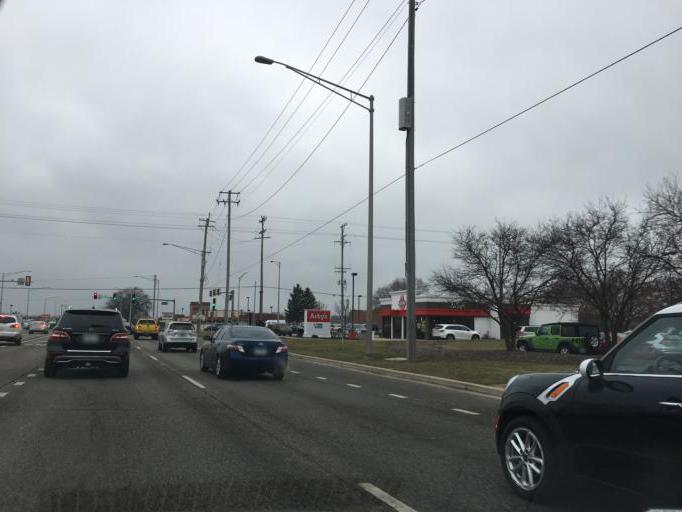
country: US
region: Illinois
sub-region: McHenry County
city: Crystal Lake
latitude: 42.2263
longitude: -88.3145
